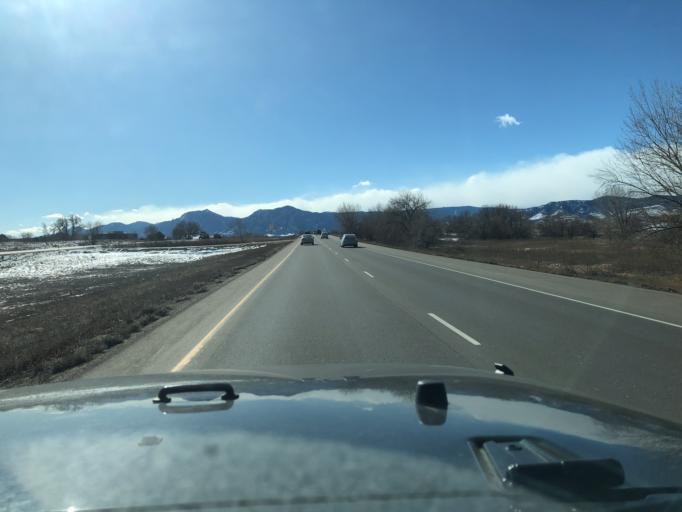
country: US
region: Colorado
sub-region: Boulder County
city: Gunbarrel
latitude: 40.0690
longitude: -105.2129
